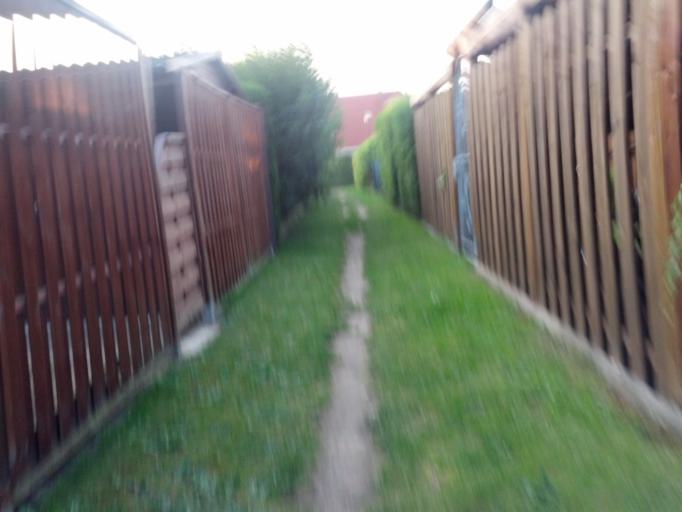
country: DE
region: Mecklenburg-Vorpommern
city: Ostseebad Kuhlungsborn
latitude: 54.1466
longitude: 11.7673
